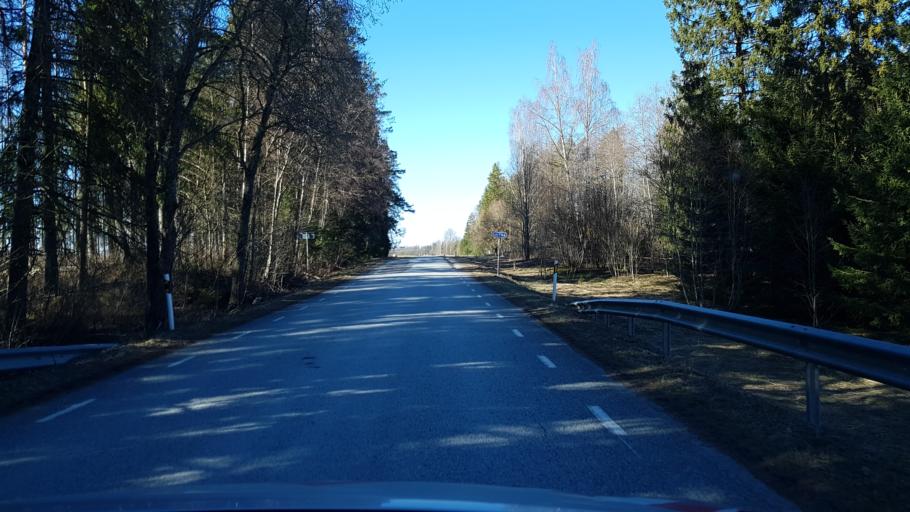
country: EE
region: Laeaene-Virumaa
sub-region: Viru-Nigula vald
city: Kunda
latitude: 59.3800
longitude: 26.5765
